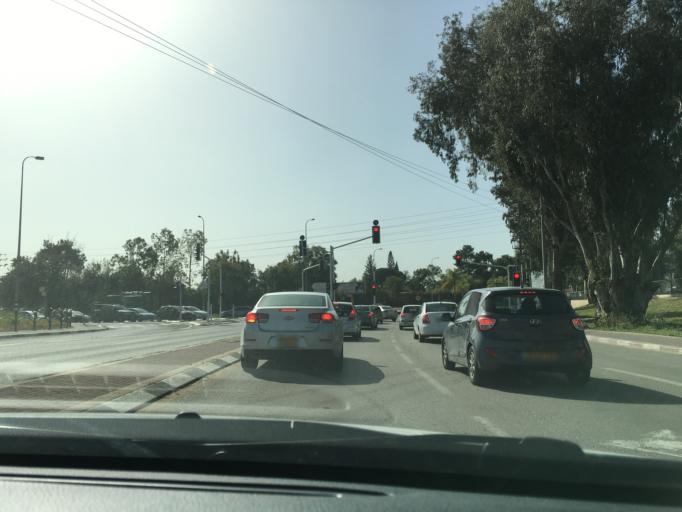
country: IL
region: Central District
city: Kfar Saba
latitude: 32.1708
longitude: 34.9292
